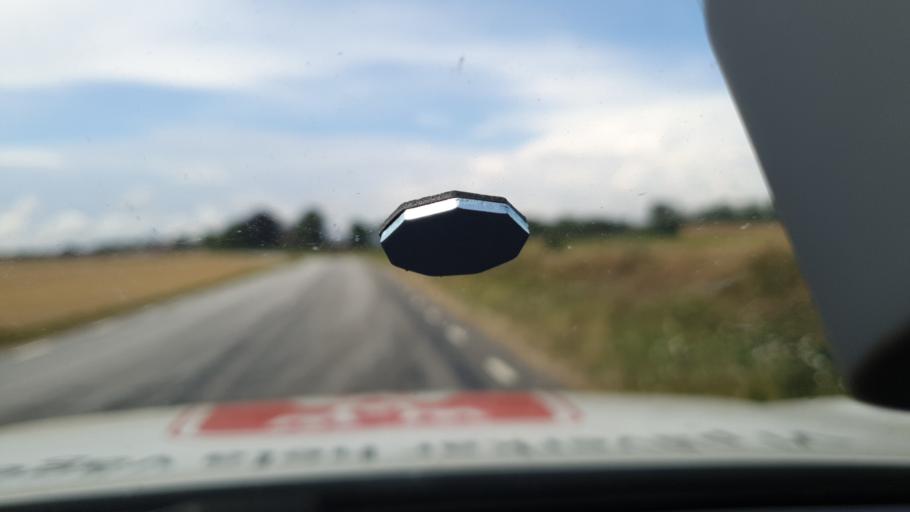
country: SE
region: Skane
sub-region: Simrishamns Kommun
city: Simrishamn
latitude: 55.4664
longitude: 14.2074
